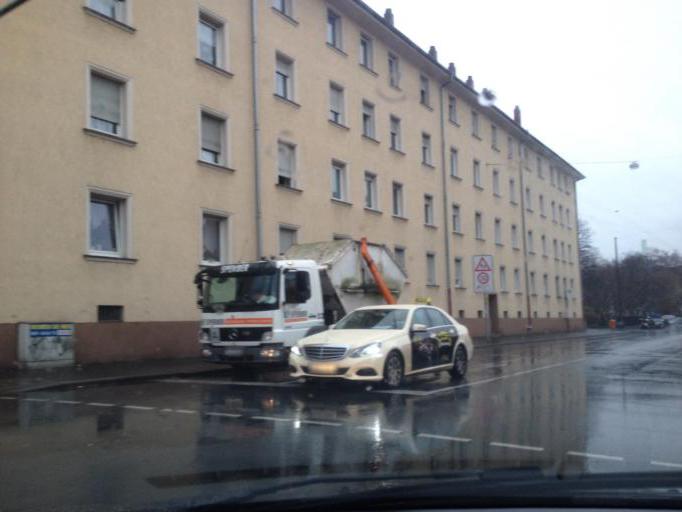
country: DE
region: Bavaria
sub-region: Regierungsbezirk Mittelfranken
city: Nuernberg
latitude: 49.4351
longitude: 11.0679
